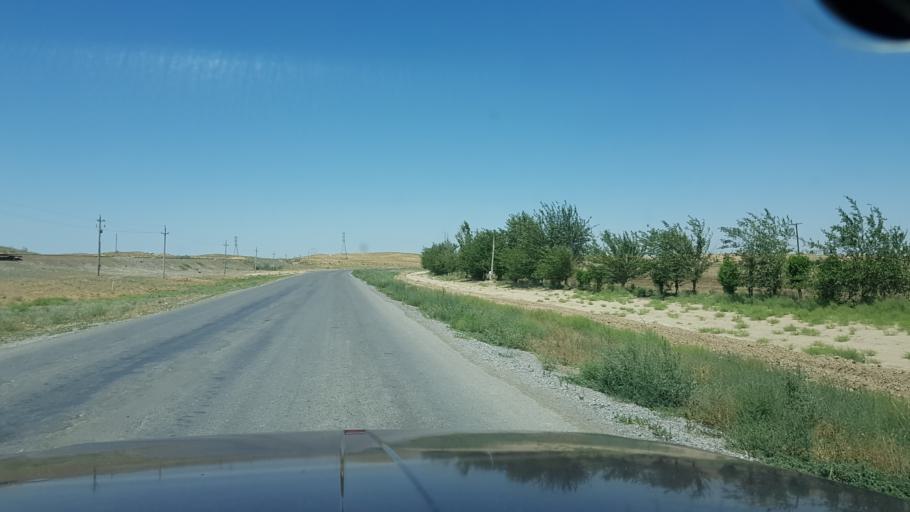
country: TM
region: Ahal
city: Annau
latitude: 37.8527
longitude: 58.7100
